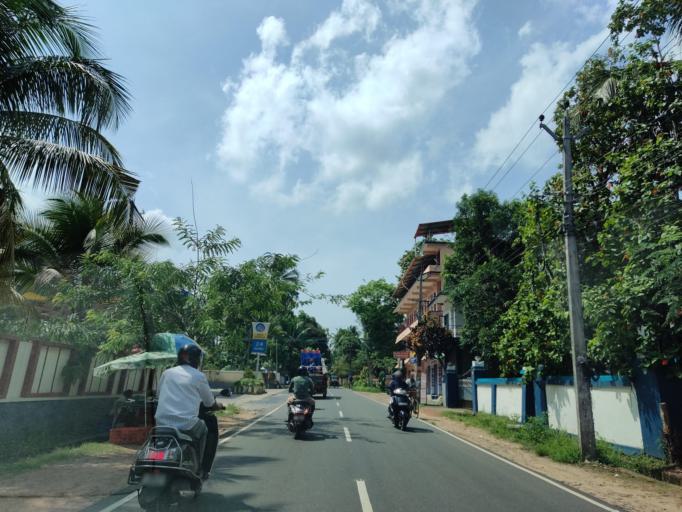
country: IN
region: Kerala
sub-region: Alappuzha
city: Mavelikara
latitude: 9.2648
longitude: 76.5408
